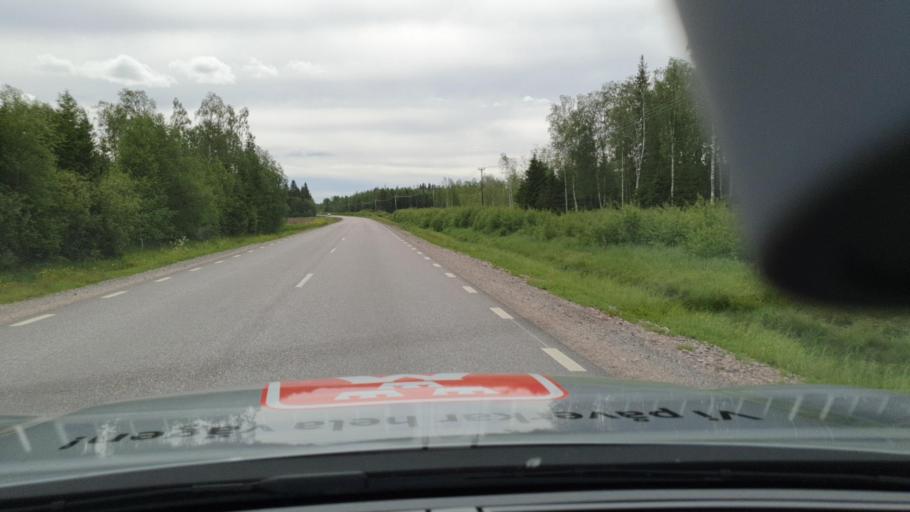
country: SE
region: Norrbotten
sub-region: Kalix Kommun
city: Kalix
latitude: 65.8994
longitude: 23.4608
